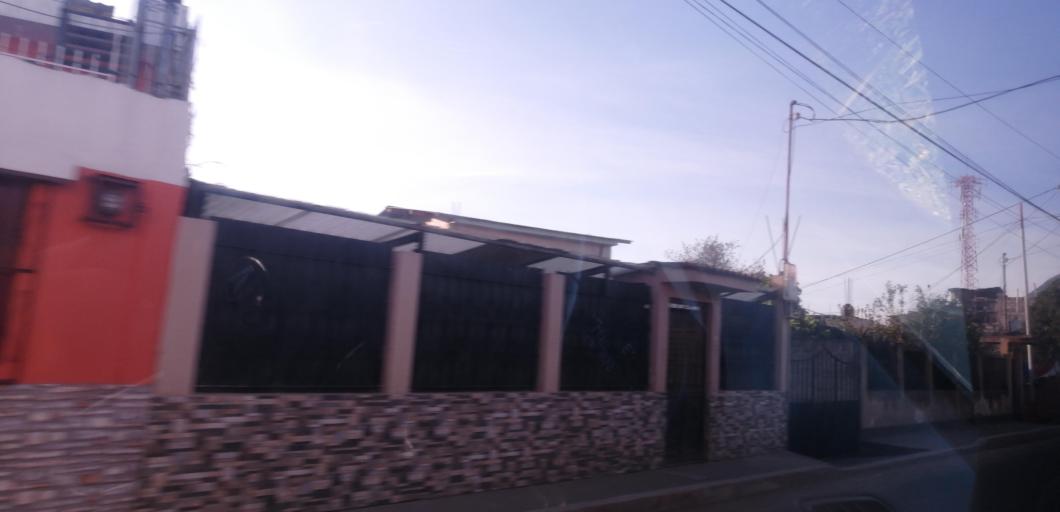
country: GT
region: Quetzaltenango
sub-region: Municipio de La Esperanza
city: La Esperanza
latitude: 14.8635
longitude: -91.5396
